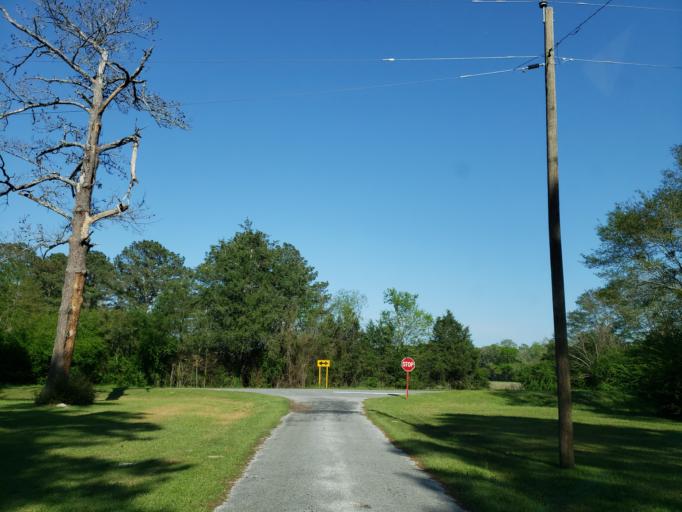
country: US
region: Mississippi
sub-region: Smith County
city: Taylorsville
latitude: 31.6894
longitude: -89.4139
